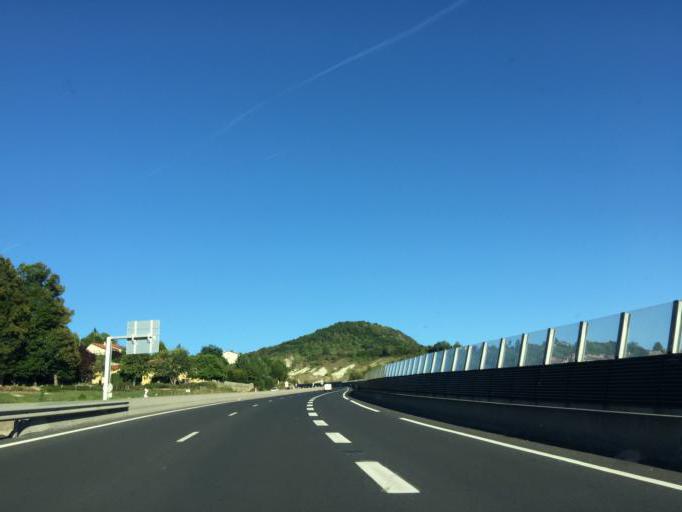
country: FR
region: Auvergne
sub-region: Departement de la Haute-Loire
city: Brives-Charensac
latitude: 45.0569
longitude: 3.9195
